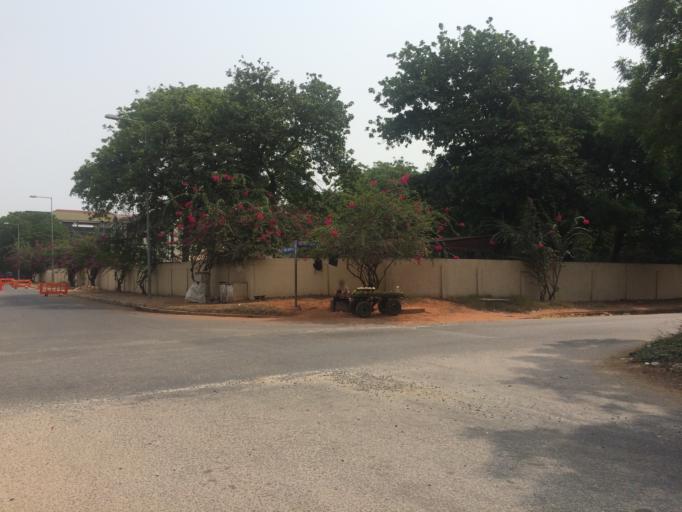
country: GH
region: Greater Accra
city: Accra
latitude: 5.5604
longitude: -0.1945
